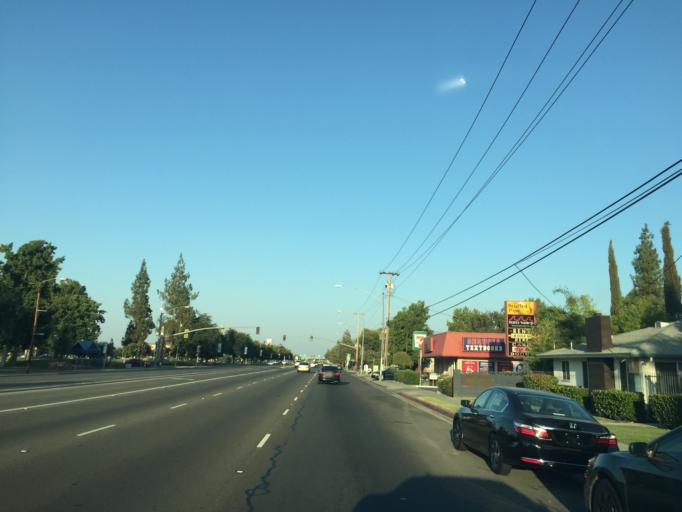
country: US
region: California
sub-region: Fresno County
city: Clovis
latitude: 36.8085
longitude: -119.7467
